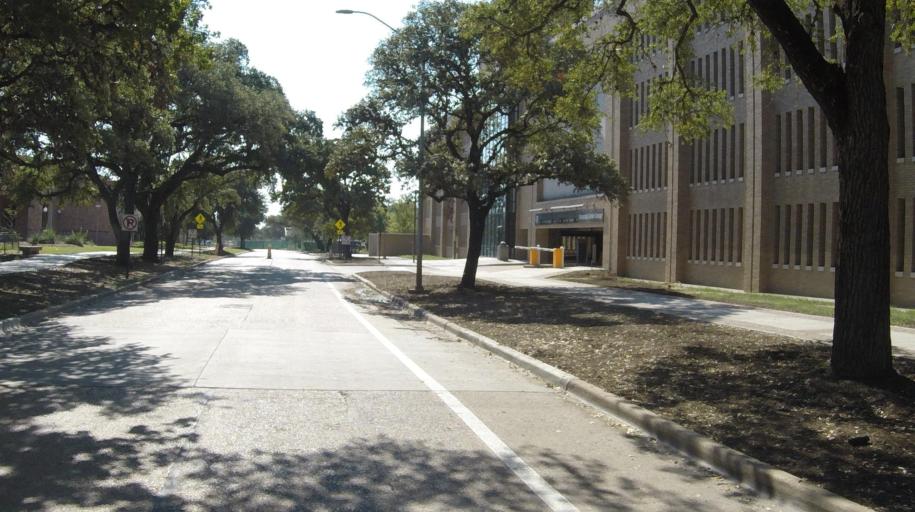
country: US
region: Texas
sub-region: Brazos County
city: College Station
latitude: 30.6127
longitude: -96.3385
